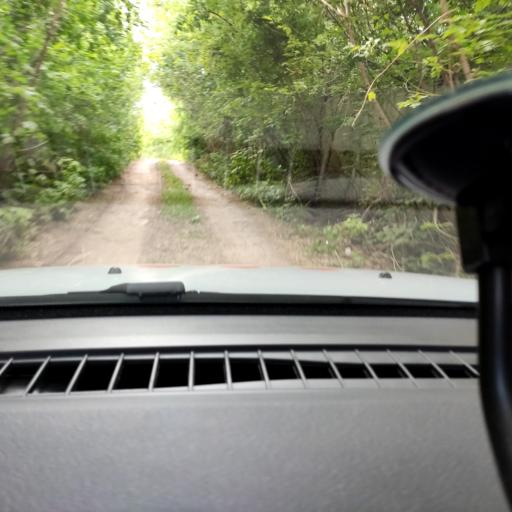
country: RU
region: Samara
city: Samara
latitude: 53.1795
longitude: 50.2179
